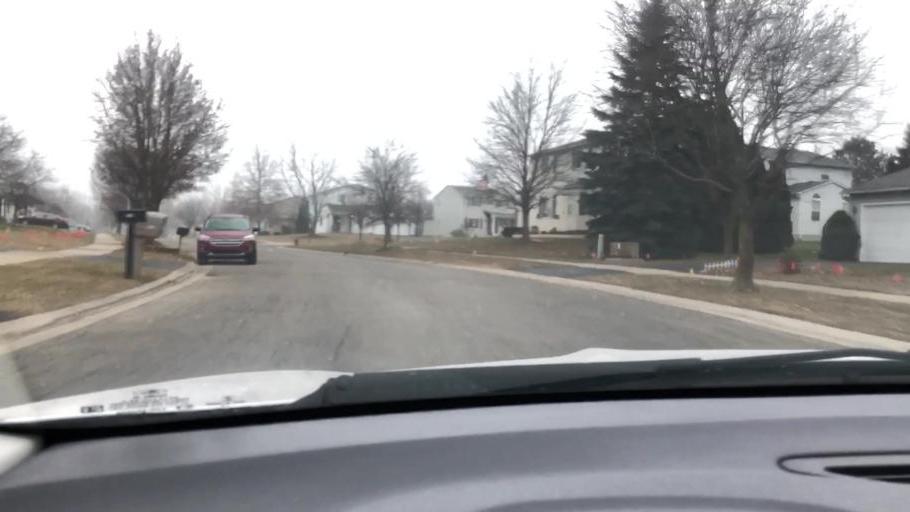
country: US
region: Michigan
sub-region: Oakland County
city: South Lyon
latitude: 42.4630
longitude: -83.6391
